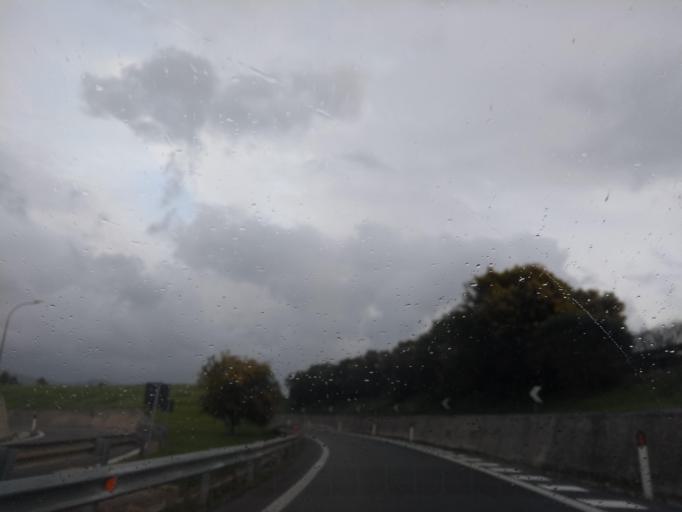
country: IT
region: Sicily
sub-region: Trapani
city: Fulgatore-Torretta
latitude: 37.9621
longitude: 12.6272
